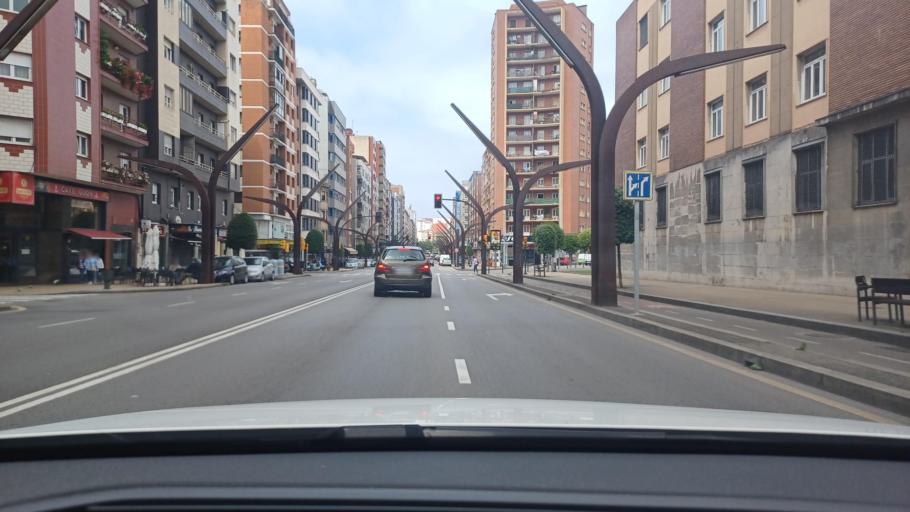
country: ES
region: Asturias
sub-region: Province of Asturias
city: Gijon
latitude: 43.5336
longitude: -5.6696
